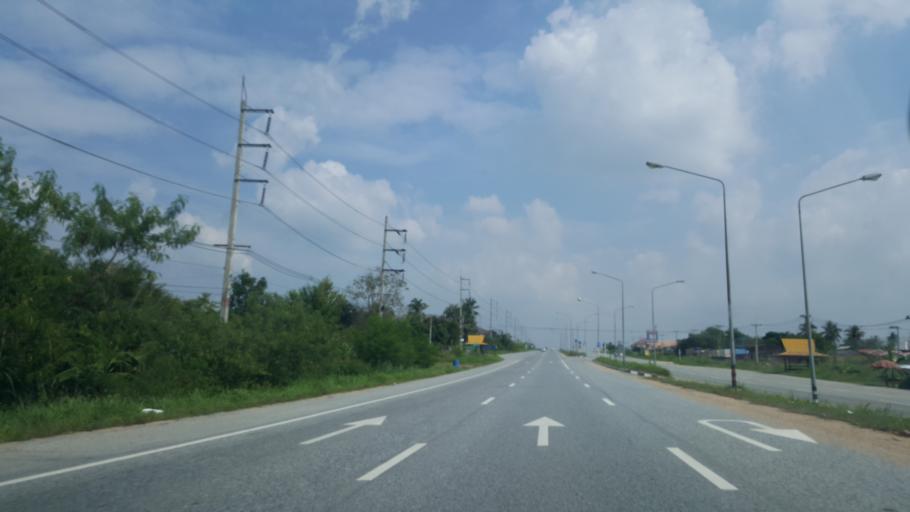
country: TH
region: Chon Buri
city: Ban Talat Bueng
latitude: 12.9411
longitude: 101.0414
